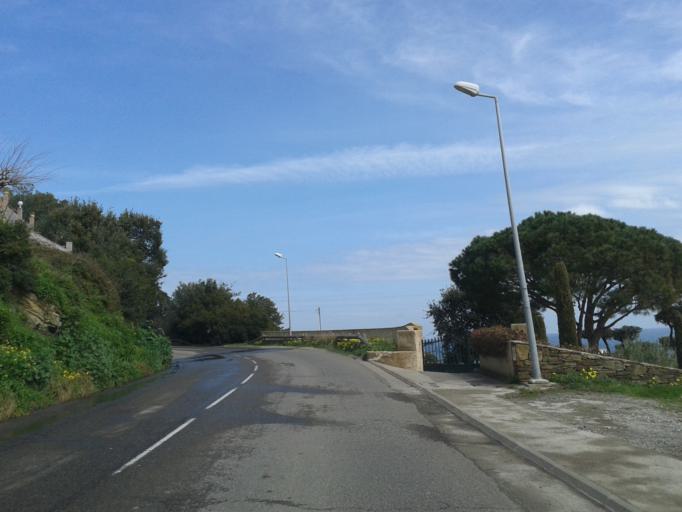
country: FR
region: Corsica
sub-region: Departement de la Haute-Corse
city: Brando
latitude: 42.7825
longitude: 9.4820
